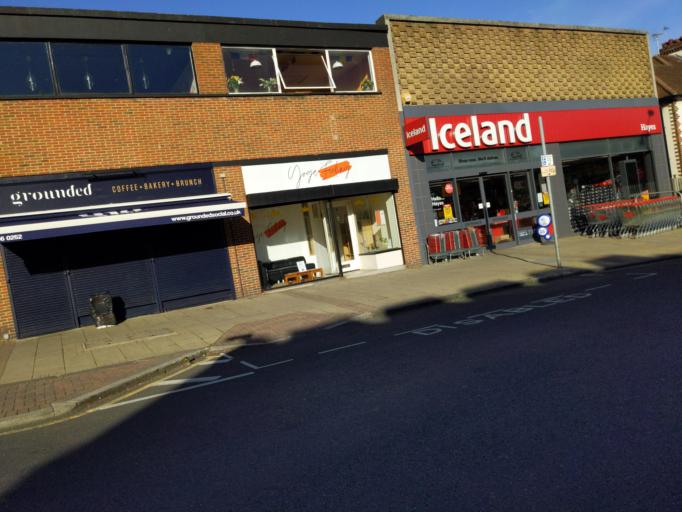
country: GB
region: England
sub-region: Greater London
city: Bromley
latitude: 51.3776
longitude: 0.0104
